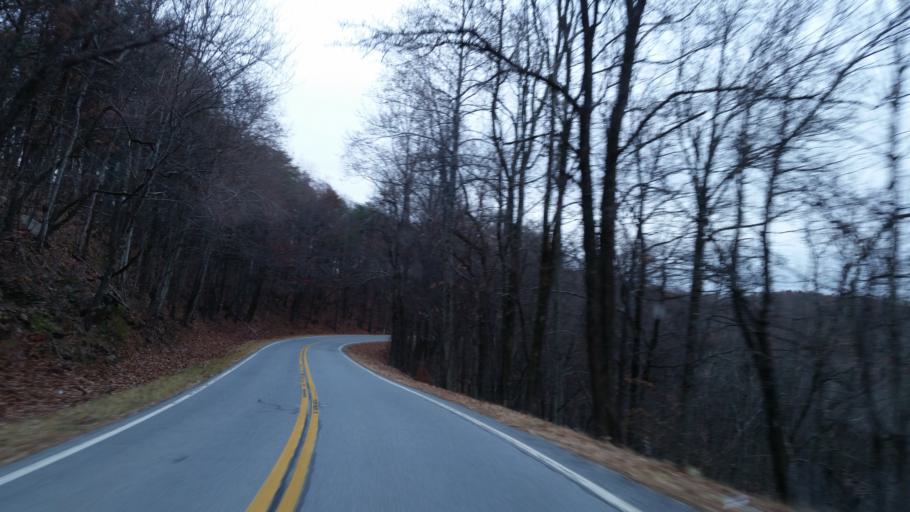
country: US
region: Georgia
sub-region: Pickens County
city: Jasper
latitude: 34.5416
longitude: -84.3149
